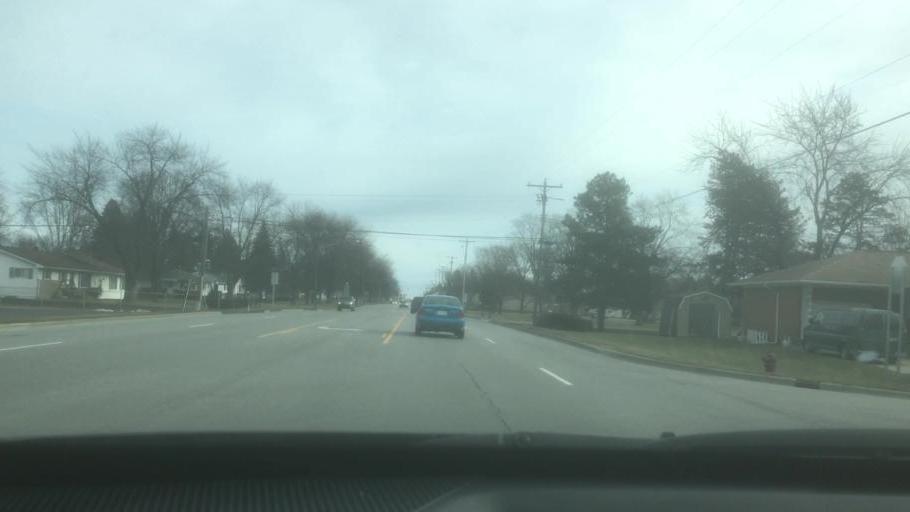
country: US
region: Michigan
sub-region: Bay County
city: Bay City
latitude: 43.6239
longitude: -83.9250
